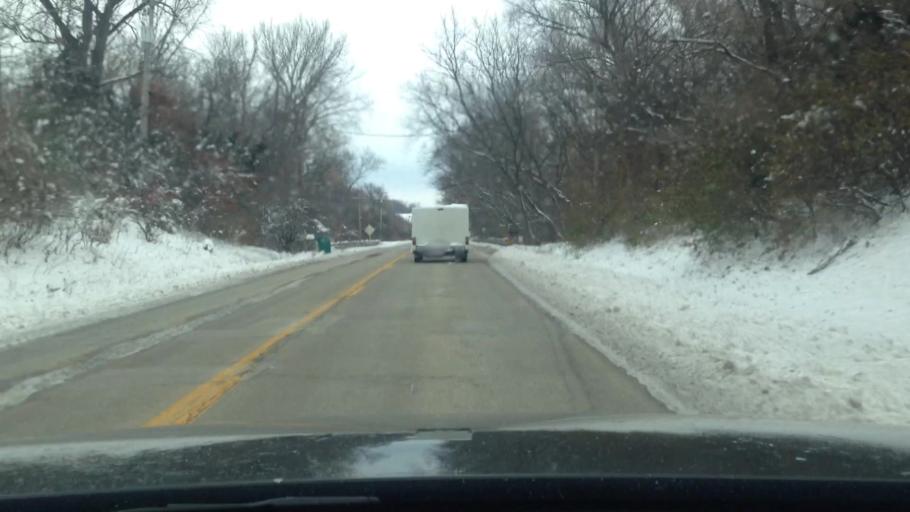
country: US
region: Illinois
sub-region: McHenry County
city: Hebron
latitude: 42.4828
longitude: -88.4425
